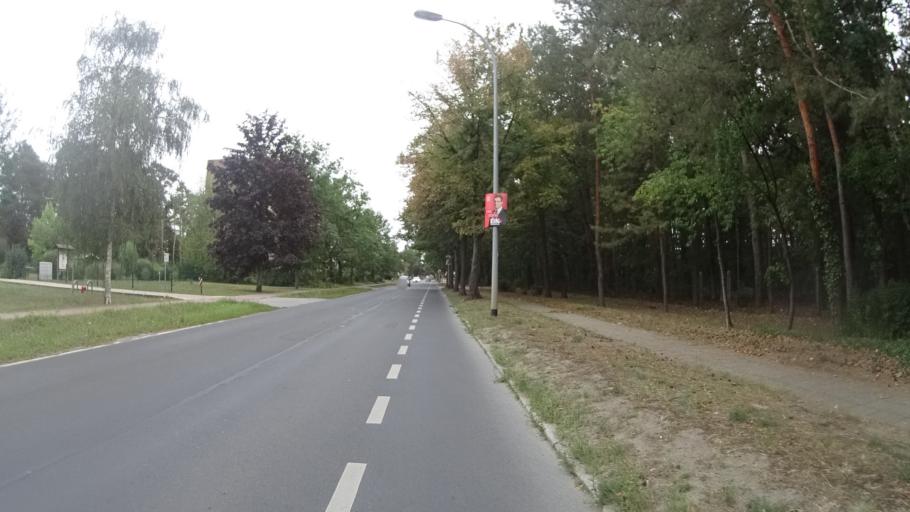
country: DE
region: Brandenburg
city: Luckenwalde
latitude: 52.1051
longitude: 13.1488
